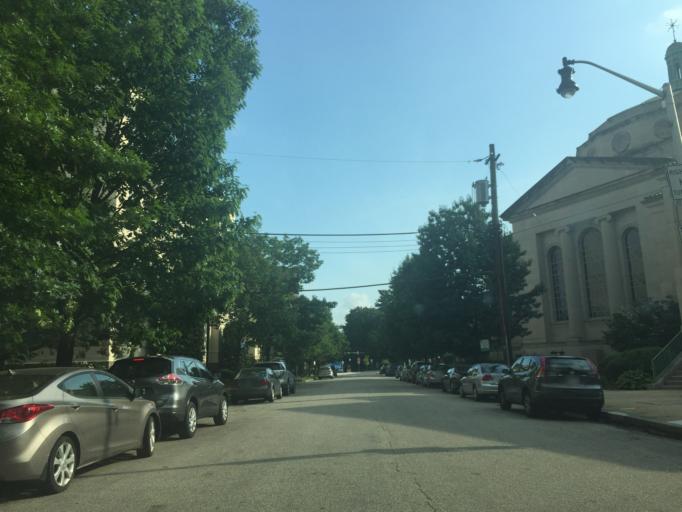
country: US
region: Maryland
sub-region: City of Baltimore
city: Baltimore
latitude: 39.3305
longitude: -76.6168
